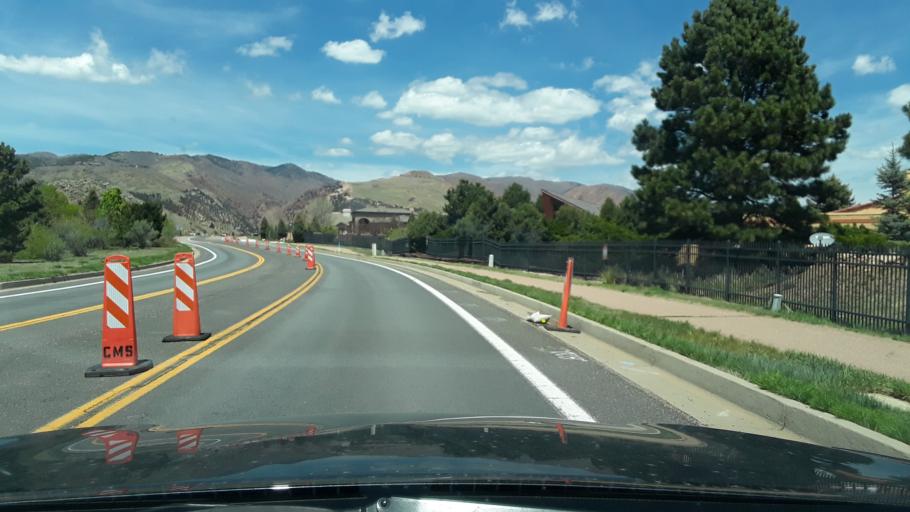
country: US
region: Colorado
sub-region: El Paso County
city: Manitou Springs
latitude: 38.8818
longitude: -104.8692
